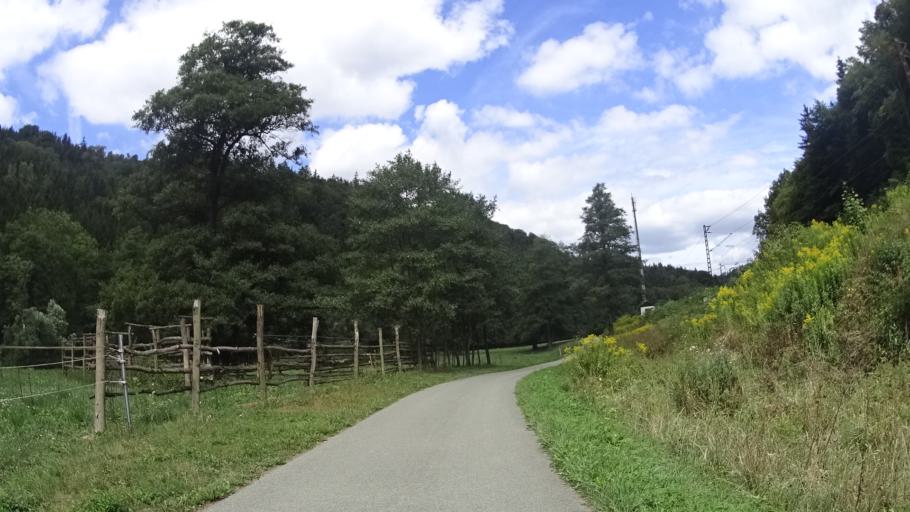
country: CZ
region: Pardubicky
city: Brandys nad Orlici
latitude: 49.9771
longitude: 16.3346
